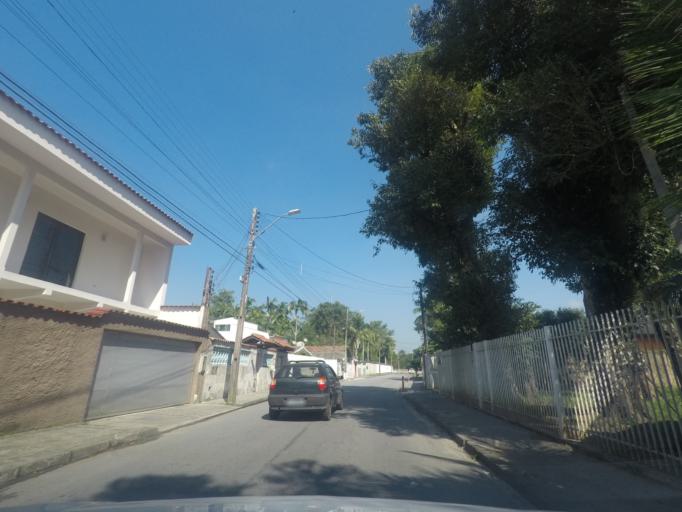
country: BR
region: Parana
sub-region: Paranagua
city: Paranagua
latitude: -25.5285
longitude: -48.5151
